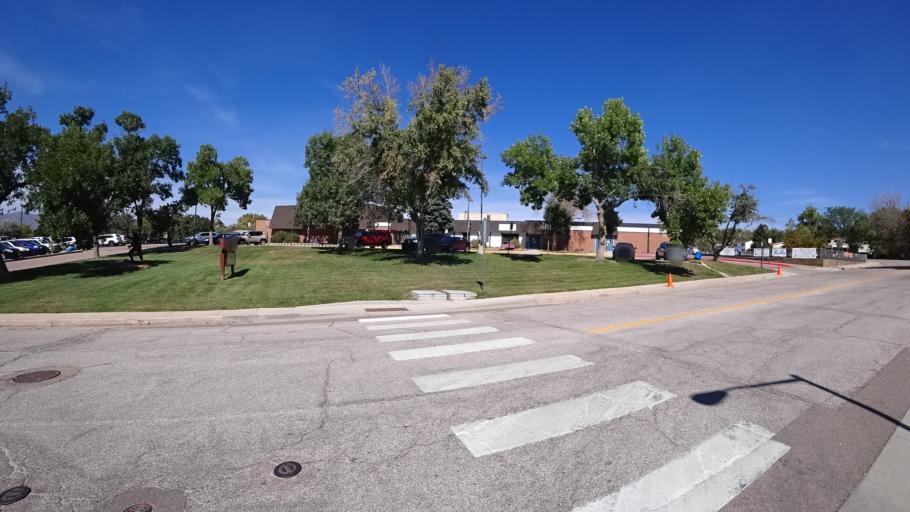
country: US
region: Colorado
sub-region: El Paso County
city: Cimarron Hills
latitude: 38.9062
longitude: -104.7706
